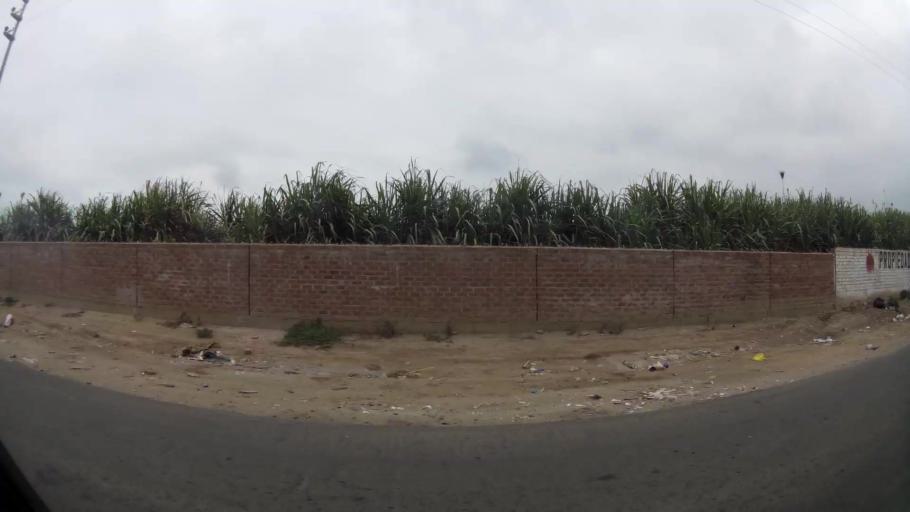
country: PE
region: La Libertad
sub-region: Provincia de Trujillo
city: Trujillo
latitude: -8.1206
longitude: -79.0478
